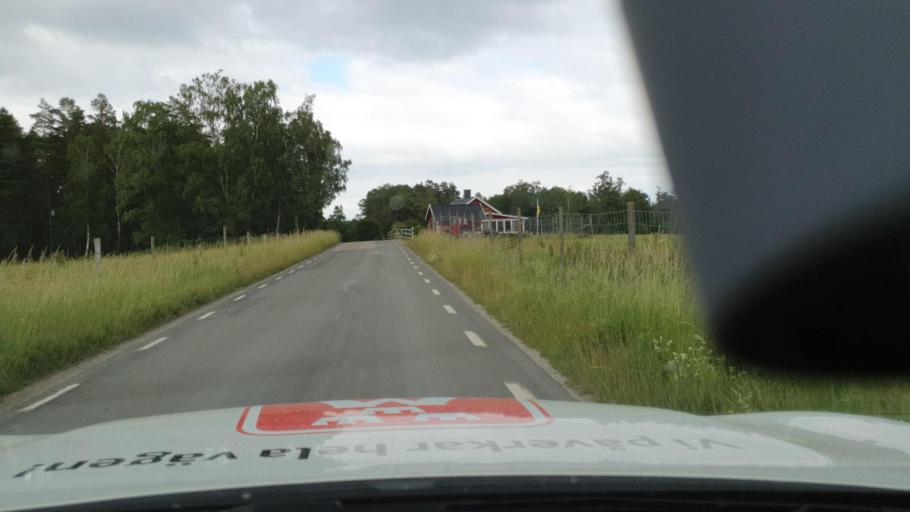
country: SE
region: Vaestra Goetaland
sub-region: Hjo Kommun
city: Hjo
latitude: 58.1727
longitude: 14.1676
